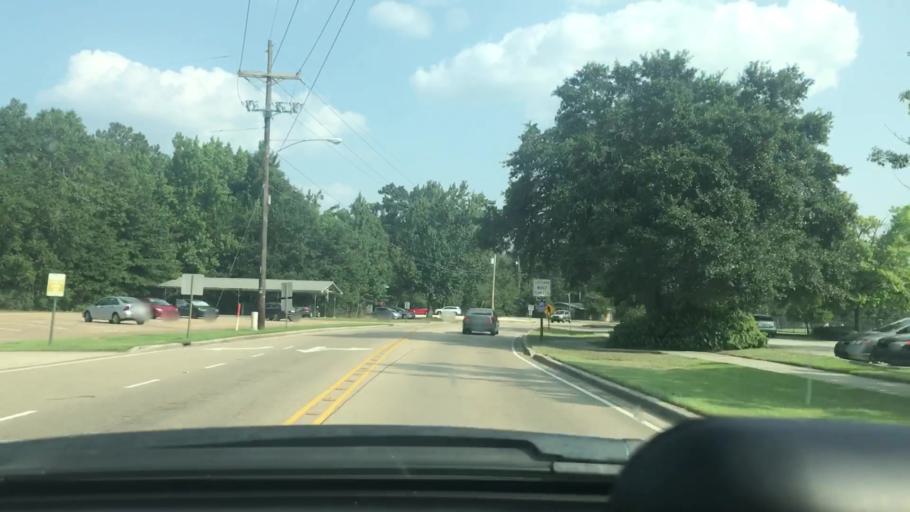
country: US
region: Louisiana
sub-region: Tangipahoa Parish
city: Hammond
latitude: 30.5189
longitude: -90.4666
